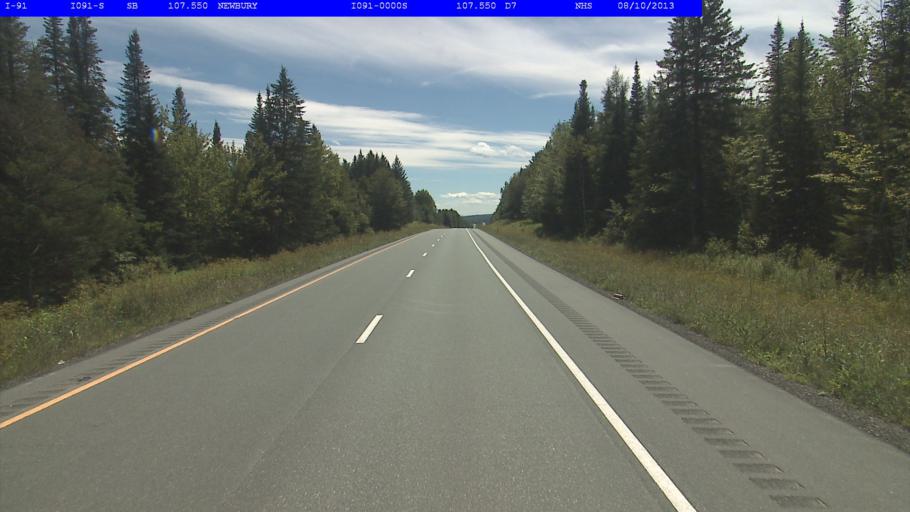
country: US
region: New Hampshire
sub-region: Grafton County
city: Woodsville
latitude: 44.1225
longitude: -72.1053
